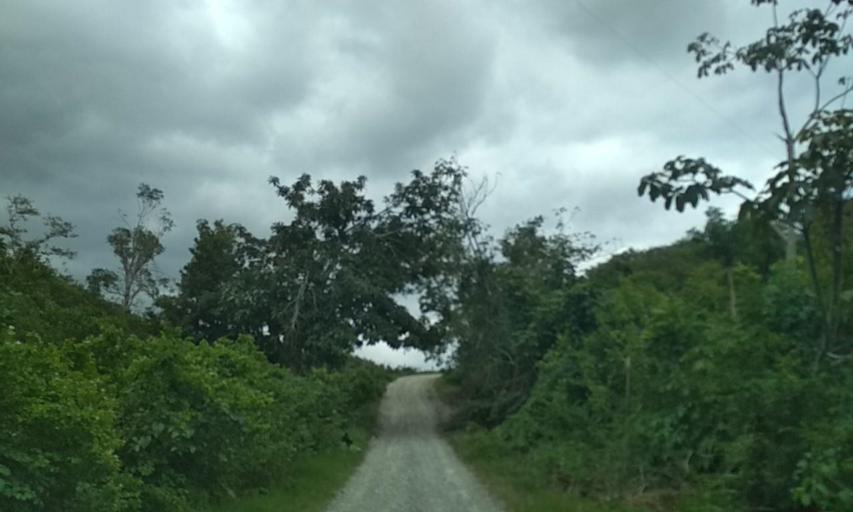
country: MX
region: Veracruz
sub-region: Papantla
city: Polutla
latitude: 20.5189
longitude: -97.2965
